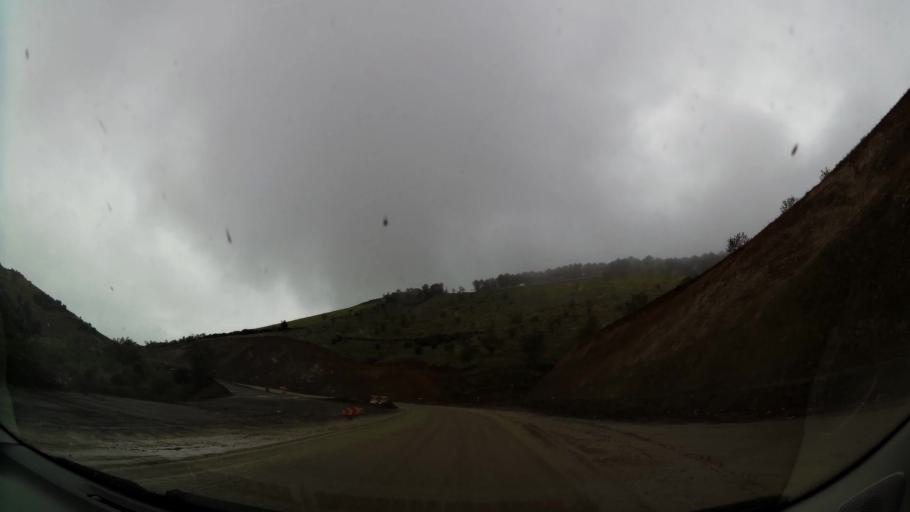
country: MA
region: Taza-Al Hoceima-Taounate
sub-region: Taza
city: Ajdir
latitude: 34.9067
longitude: -3.7943
